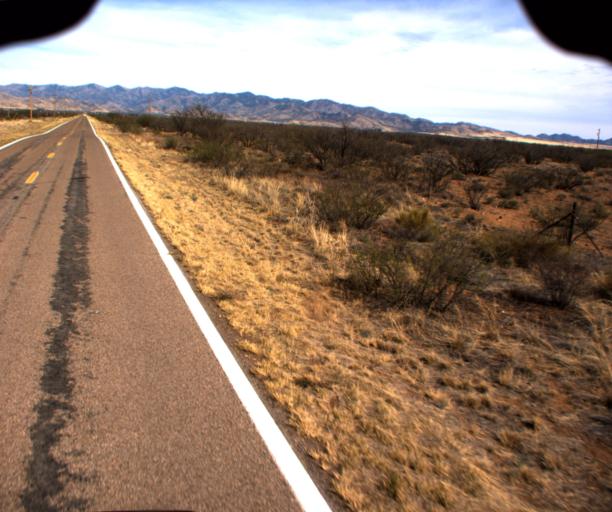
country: US
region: Arizona
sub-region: Cochise County
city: Willcox
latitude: 31.8760
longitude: -109.5468
